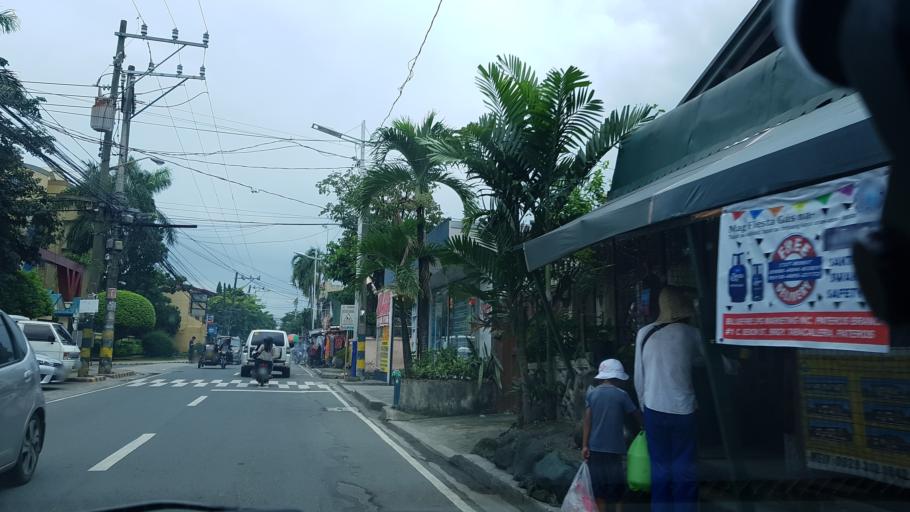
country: PH
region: Calabarzon
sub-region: Province of Rizal
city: Pateros
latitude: 14.5367
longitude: 121.0692
